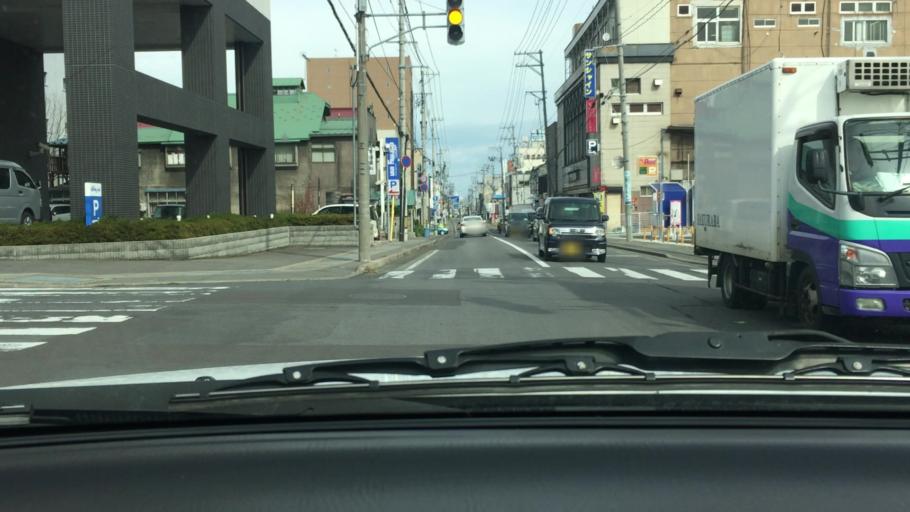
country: JP
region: Aomori
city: Hirosaki
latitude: 40.6004
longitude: 140.4688
